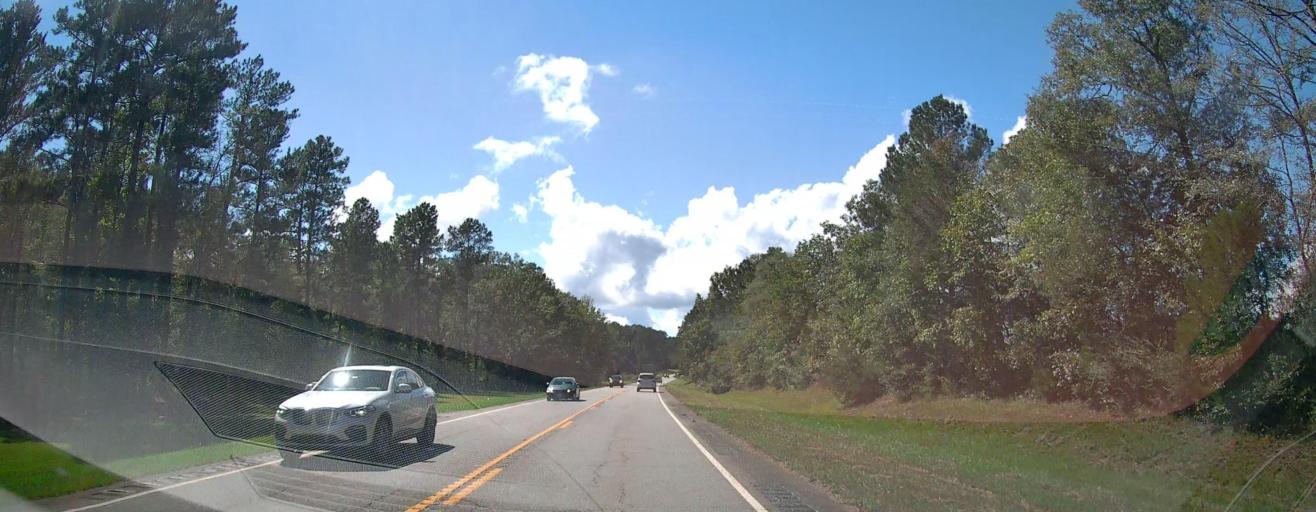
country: US
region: Georgia
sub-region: Jones County
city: Gray
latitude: 33.0404
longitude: -83.4000
